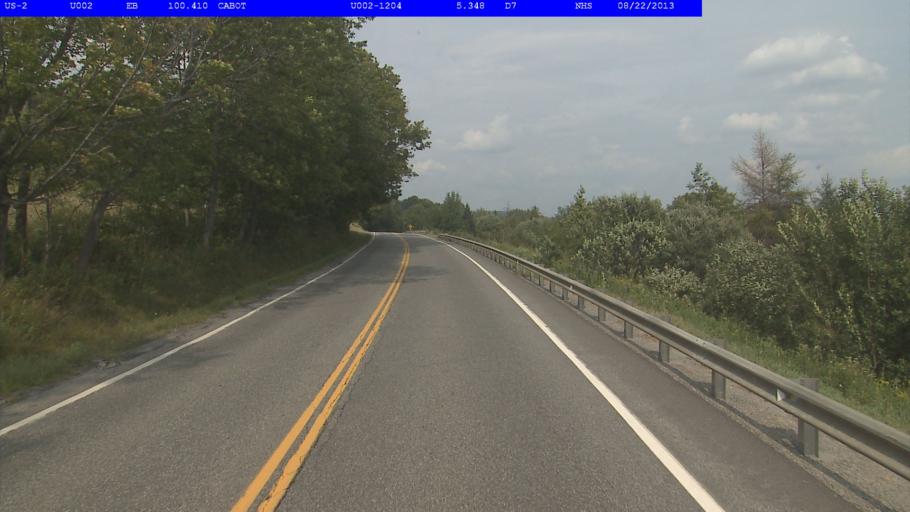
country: US
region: Vermont
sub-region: Caledonia County
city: Hardwick
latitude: 44.3956
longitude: -72.2399
